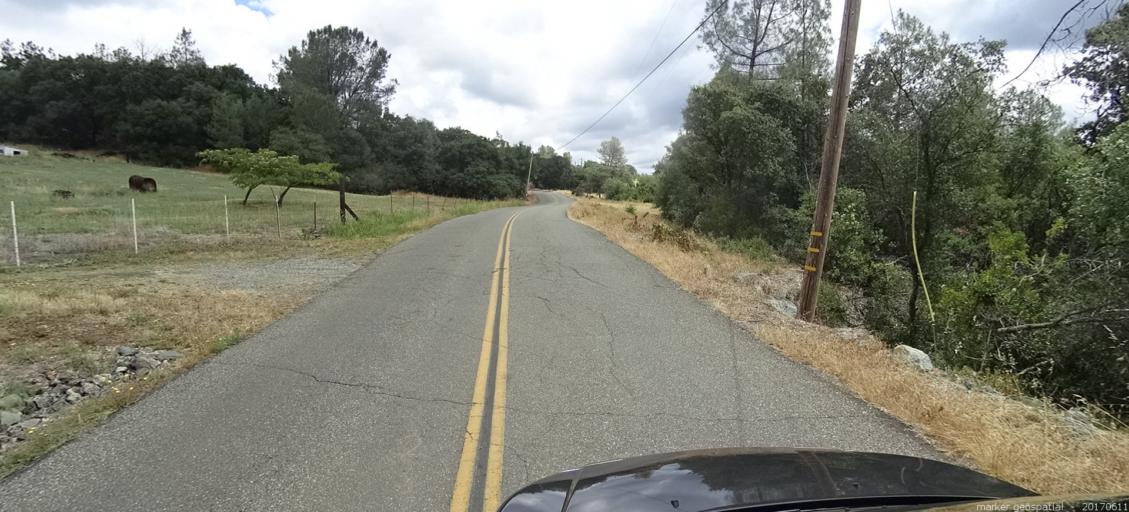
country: US
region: California
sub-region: Butte County
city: Oroville
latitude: 39.6434
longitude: -121.5404
